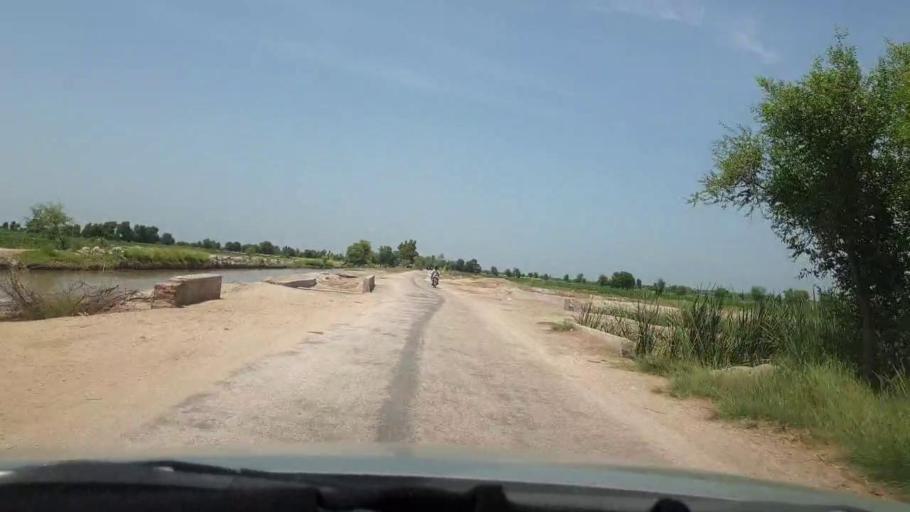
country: PK
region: Sindh
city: Pano Aqil
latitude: 27.6647
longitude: 69.1079
